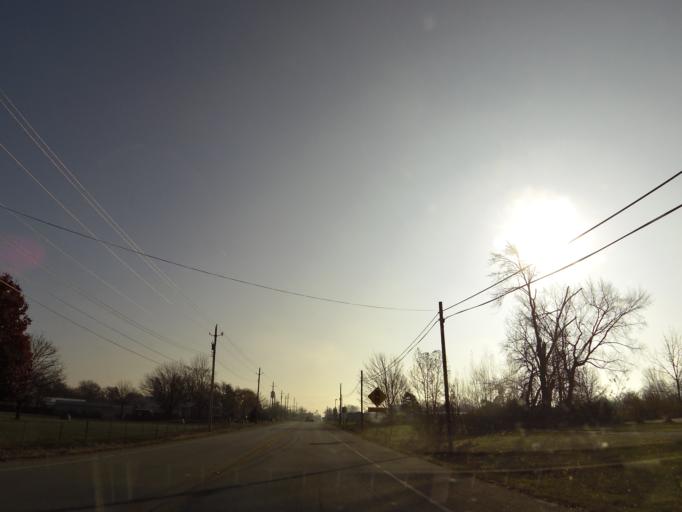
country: US
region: Indiana
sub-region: Marion County
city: Clermont
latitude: 39.8188
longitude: -86.3308
